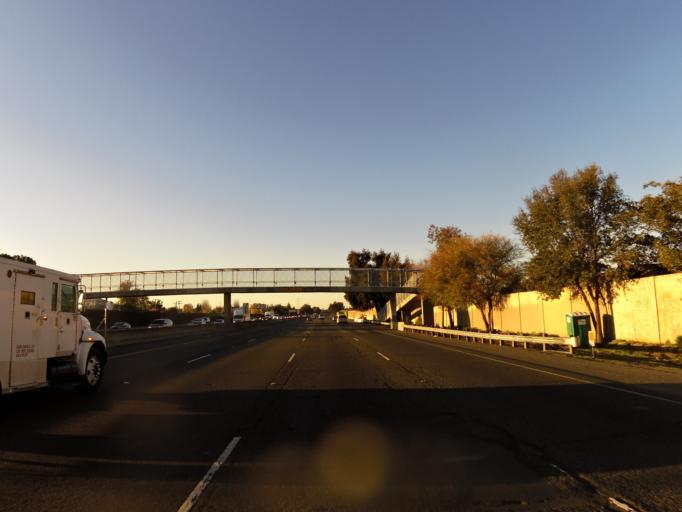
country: US
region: California
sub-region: Sacramento County
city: Parkway
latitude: 38.5020
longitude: -121.4521
